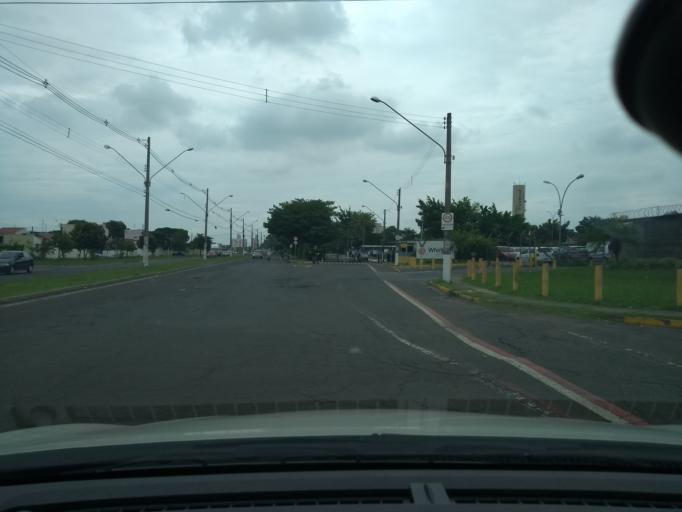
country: BR
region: Sao Paulo
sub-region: Rio Claro
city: Rio Claro
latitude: -22.3772
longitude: -47.5457
